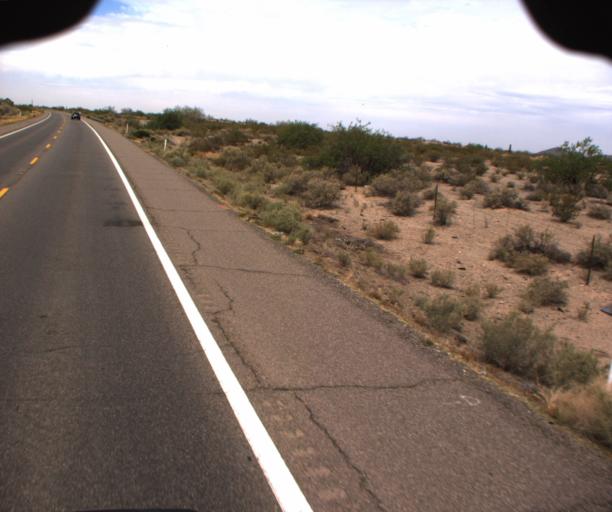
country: US
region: Arizona
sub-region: Pinal County
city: Sacaton
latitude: 33.1183
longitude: -111.7298
